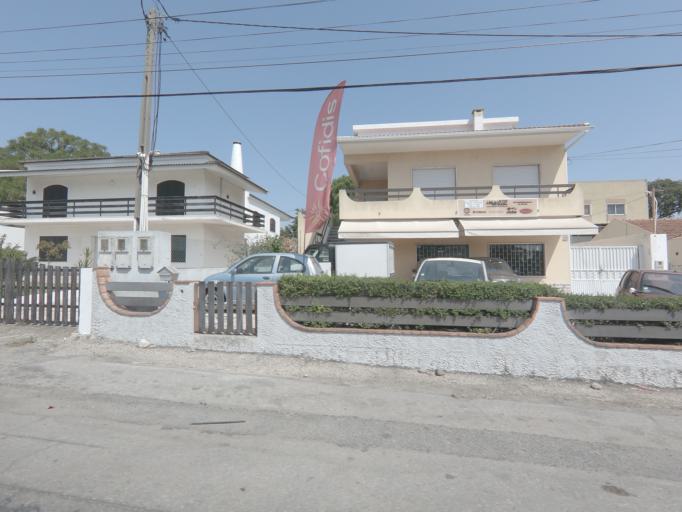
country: PT
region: Setubal
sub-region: Palmela
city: Palmela
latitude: 38.5627
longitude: -8.8881
